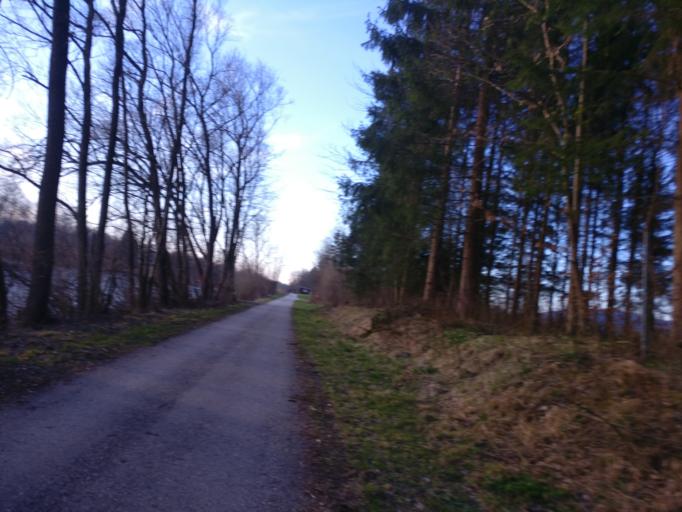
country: DE
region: Bavaria
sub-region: Upper Bavaria
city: Freilassing
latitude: 47.8518
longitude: 13.0054
